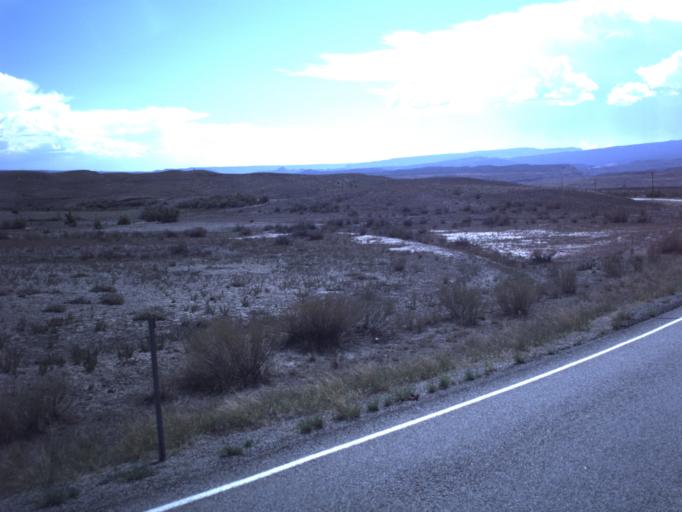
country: US
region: Utah
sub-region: Grand County
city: Moab
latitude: 38.8827
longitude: -109.3121
